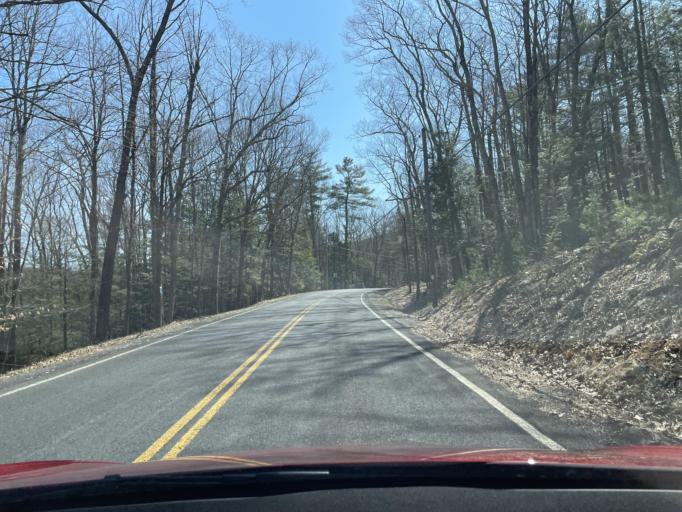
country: US
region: New York
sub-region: Ulster County
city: Shokan
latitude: 42.0128
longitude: -74.1700
